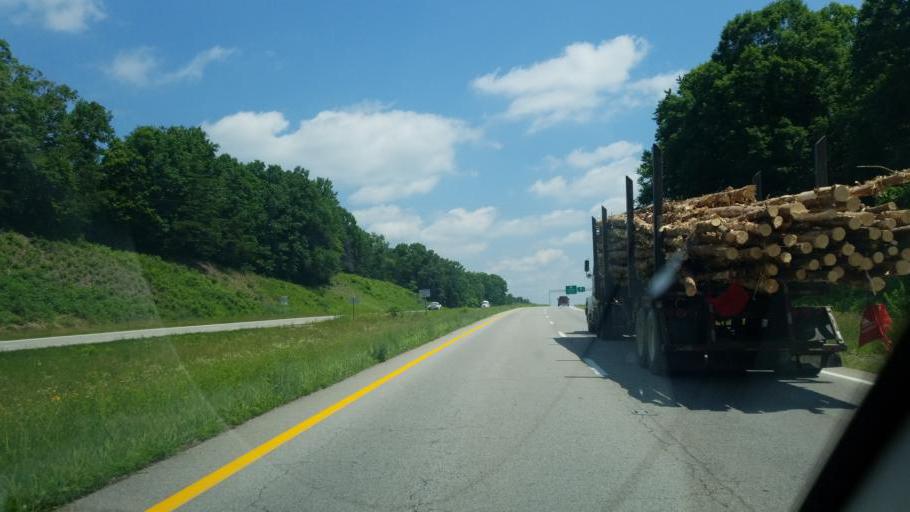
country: US
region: Virginia
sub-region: Pittsylvania County
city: Hurt
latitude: 37.1084
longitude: -79.3308
